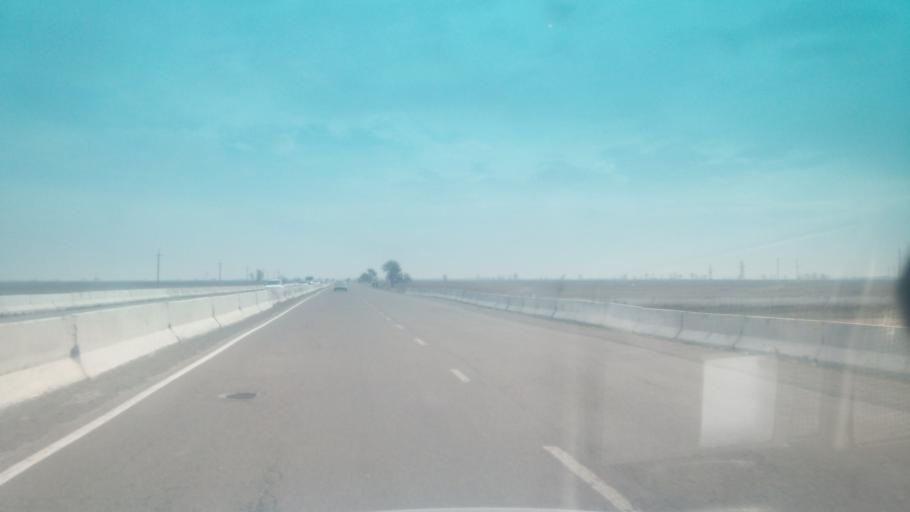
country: KZ
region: Ongtustik Qazaqstan
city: Myrzakent
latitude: 40.5215
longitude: 68.4619
